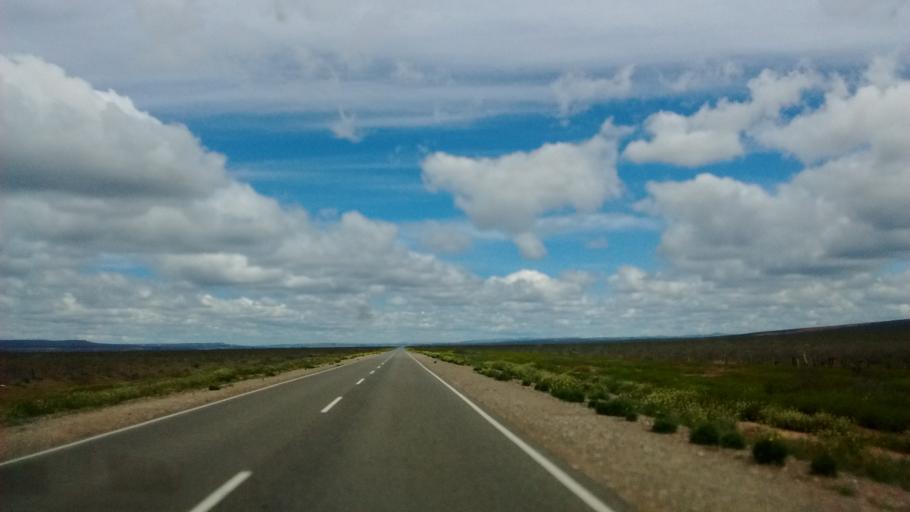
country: AR
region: Neuquen
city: Piedra del Aguila
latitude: -39.7910
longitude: -69.6742
